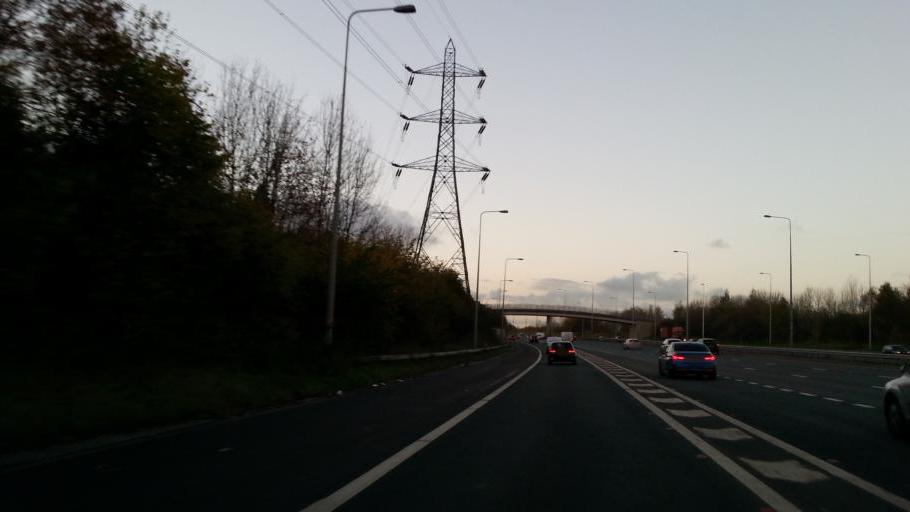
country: GB
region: England
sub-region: Borough of Rochdale
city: Middleton
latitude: 53.5365
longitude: -2.2101
